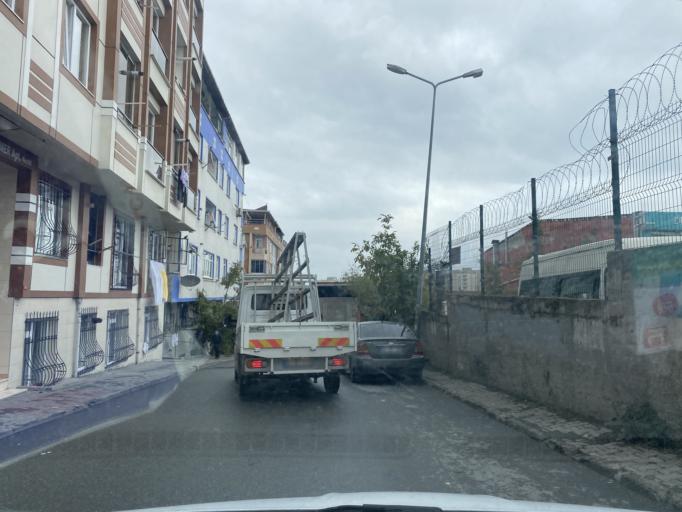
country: TR
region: Istanbul
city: Esenyurt
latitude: 41.0185
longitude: 28.6920
